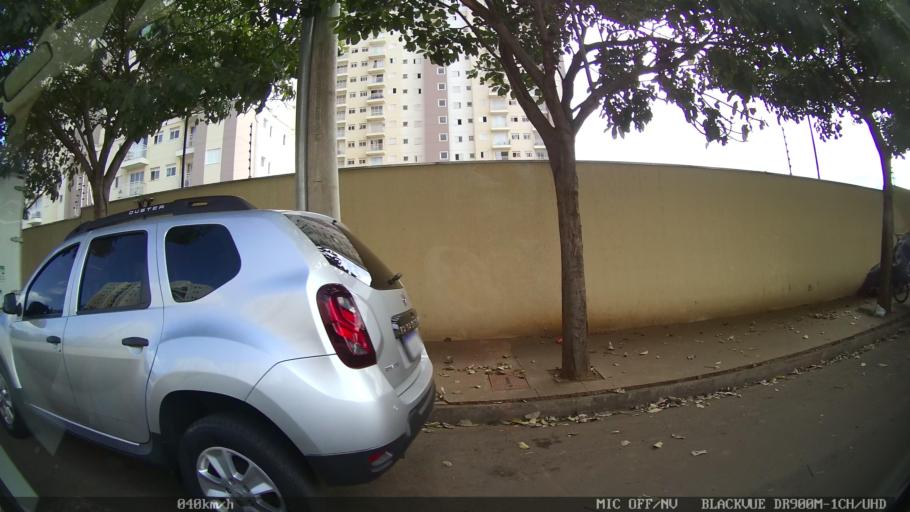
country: BR
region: Sao Paulo
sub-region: Americana
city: Americana
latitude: -22.7225
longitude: -47.3174
